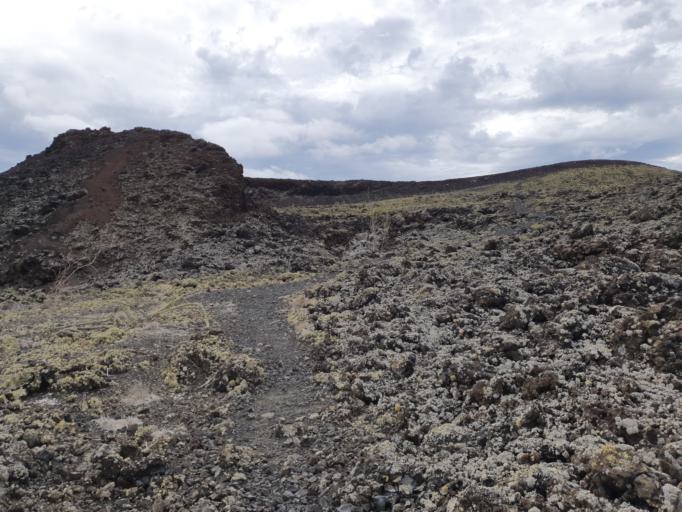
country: ES
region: Canary Islands
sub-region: Provincia de Las Palmas
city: Tinajo
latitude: 29.0226
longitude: -13.7113
